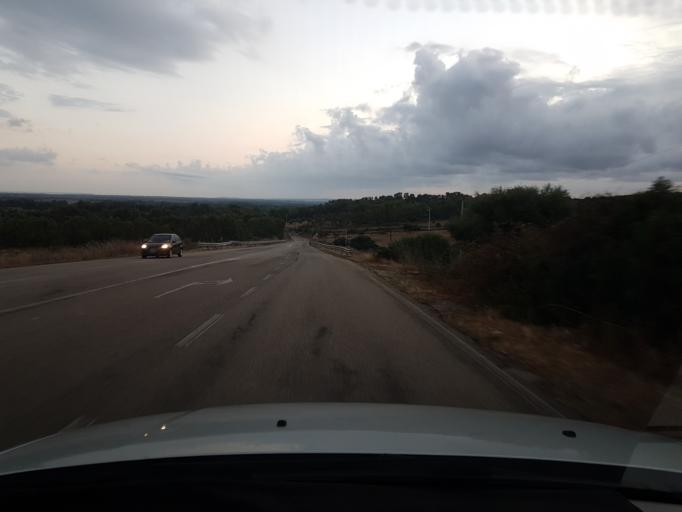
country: IT
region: Sardinia
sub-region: Provincia di Oristano
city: Milis
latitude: 40.0540
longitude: 8.6342
